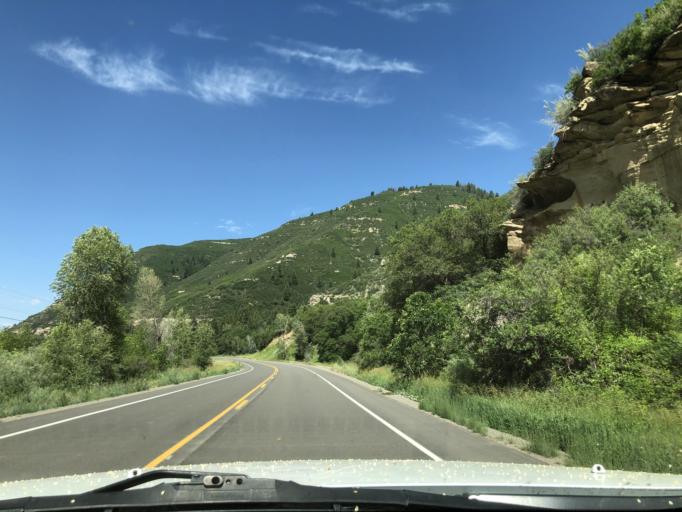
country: US
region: Colorado
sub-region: Delta County
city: Paonia
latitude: 38.9384
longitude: -107.3774
